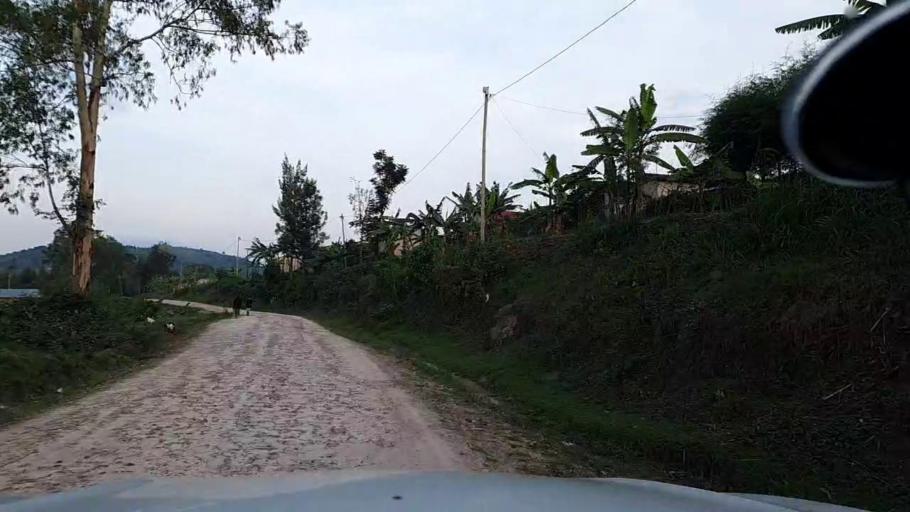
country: RW
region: Southern Province
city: Nyanza
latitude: -2.2159
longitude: 29.6371
